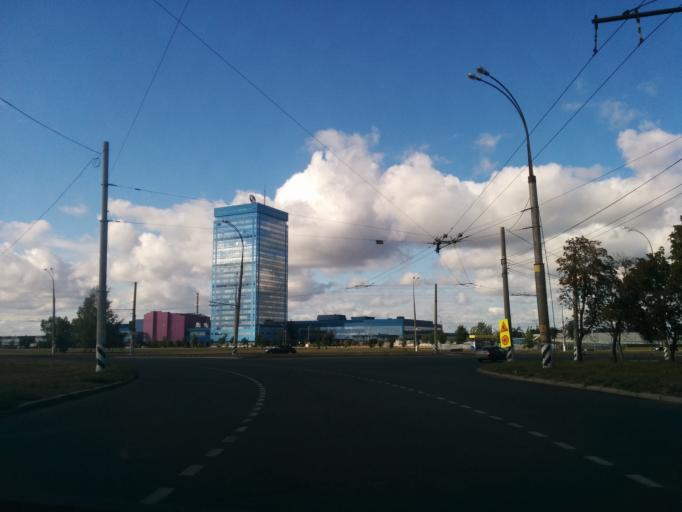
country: RU
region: Samara
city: Tol'yatti
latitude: 53.5524
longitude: 49.2681
